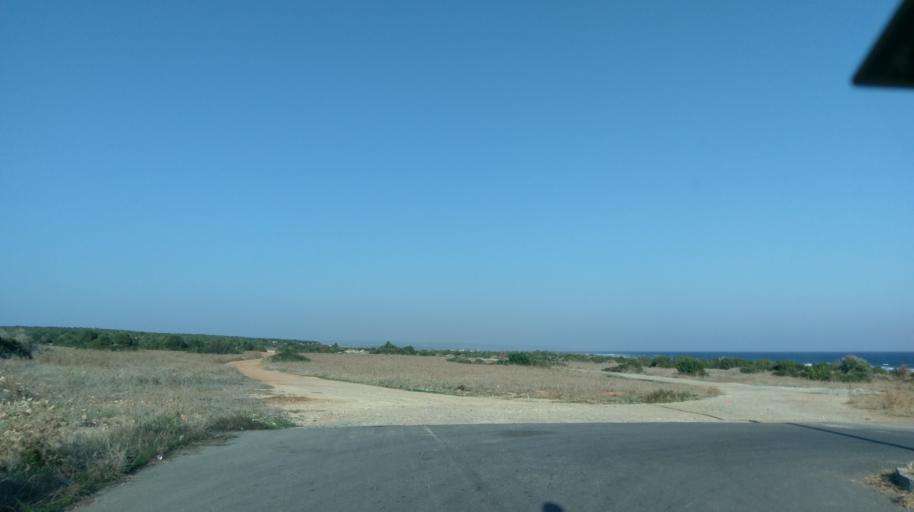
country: CY
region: Ammochostos
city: Leonarisso
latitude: 35.3850
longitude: 34.0962
